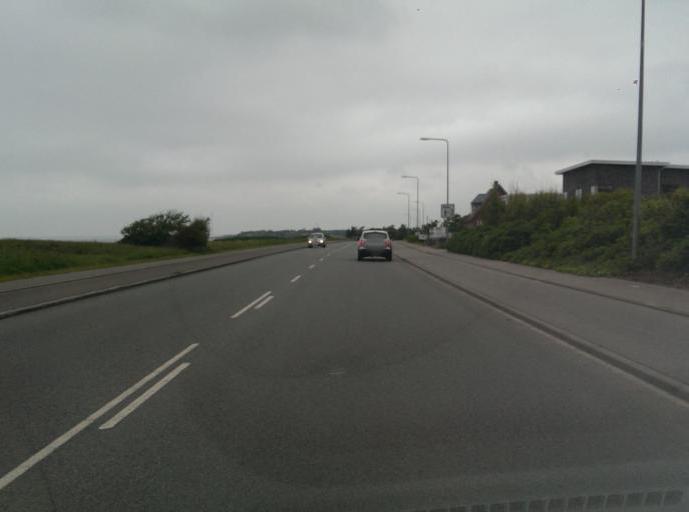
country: DK
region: South Denmark
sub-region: Fano Kommune
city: Nordby
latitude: 55.5047
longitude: 8.3852
